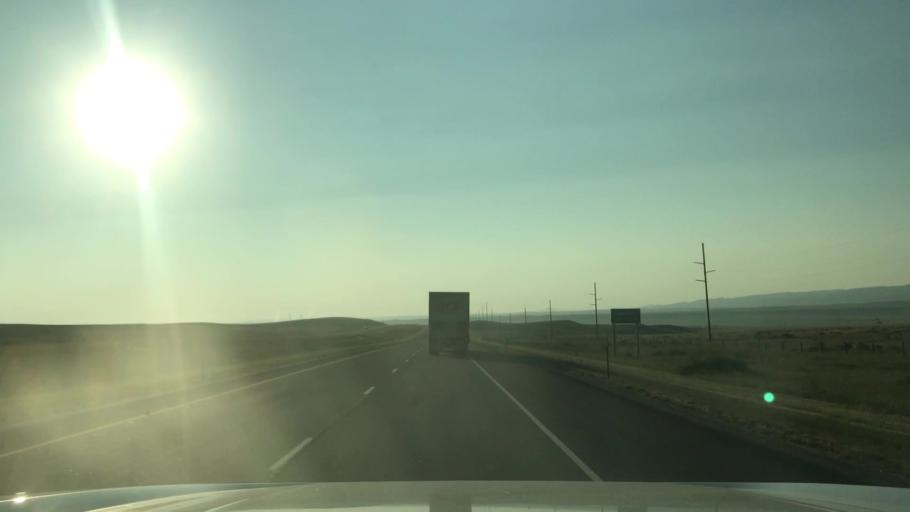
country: US
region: Wyoming
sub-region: Converse County
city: Glenrock
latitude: 42.8409
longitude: -105.9263
